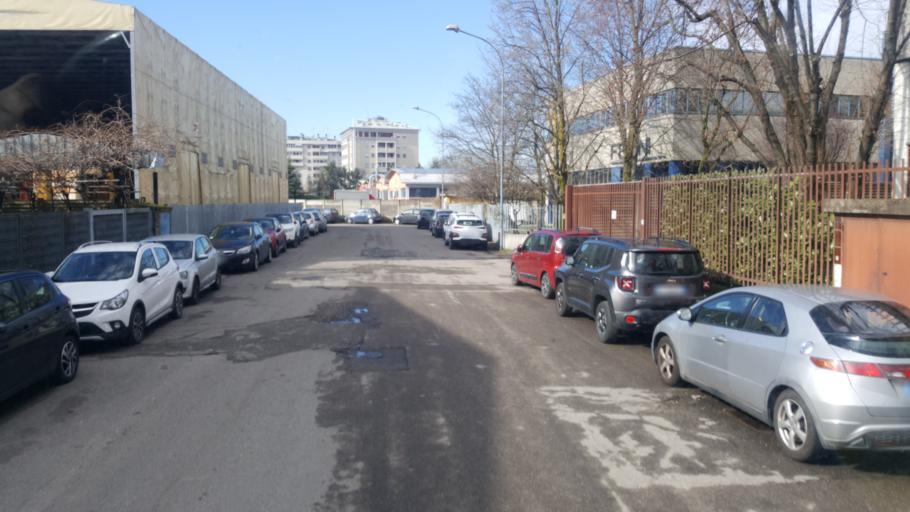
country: IT
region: Lombardy
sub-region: Citta metropolitana di Milano
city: Fizzonasco
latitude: 45.3746
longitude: 9.1825
